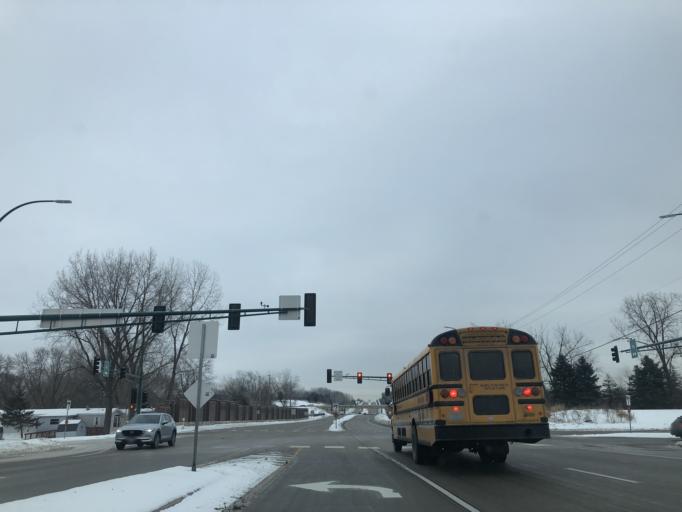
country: US
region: Minnesota
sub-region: Ramsey County
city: New Brighton
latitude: 45.0791
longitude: -93.1827
